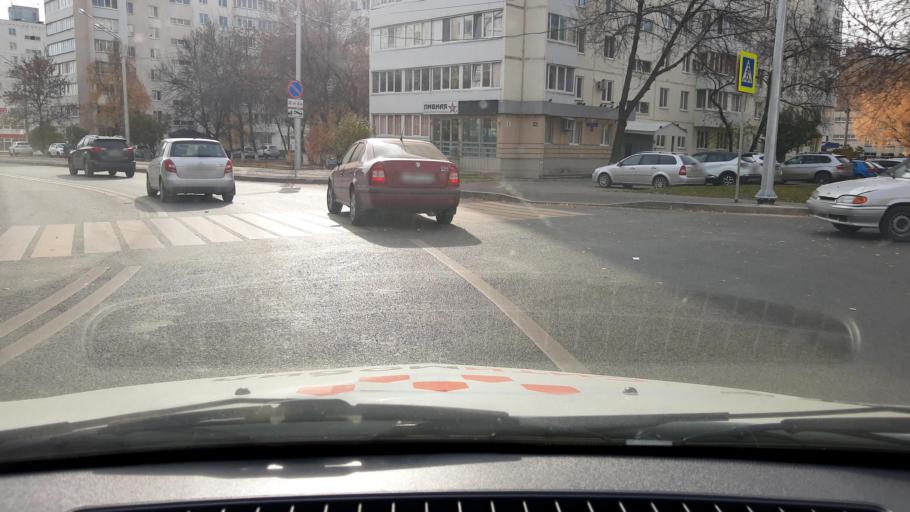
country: RU
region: Bashkortostan
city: Ufa
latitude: 54.7683
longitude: 56.0259
